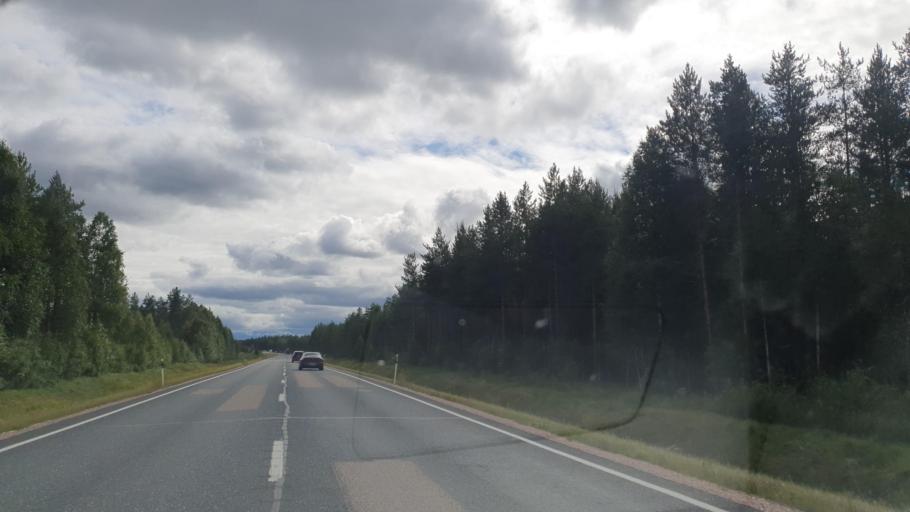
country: FI
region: Kainuu
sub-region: Kajaani
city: Kajaani
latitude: 64.0752
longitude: 27.4527
